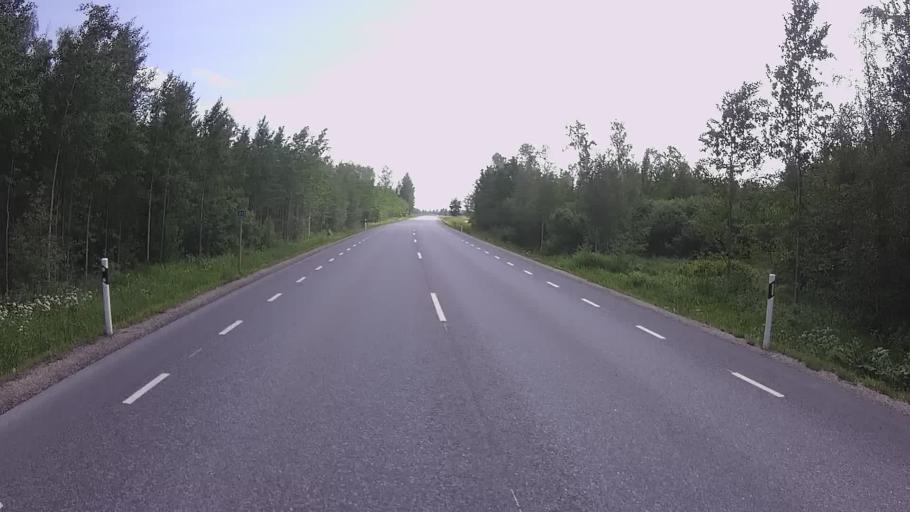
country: EE
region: Tartu
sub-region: UElenurme vald
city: Ulenurme
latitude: 58.1796
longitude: 26.8413
